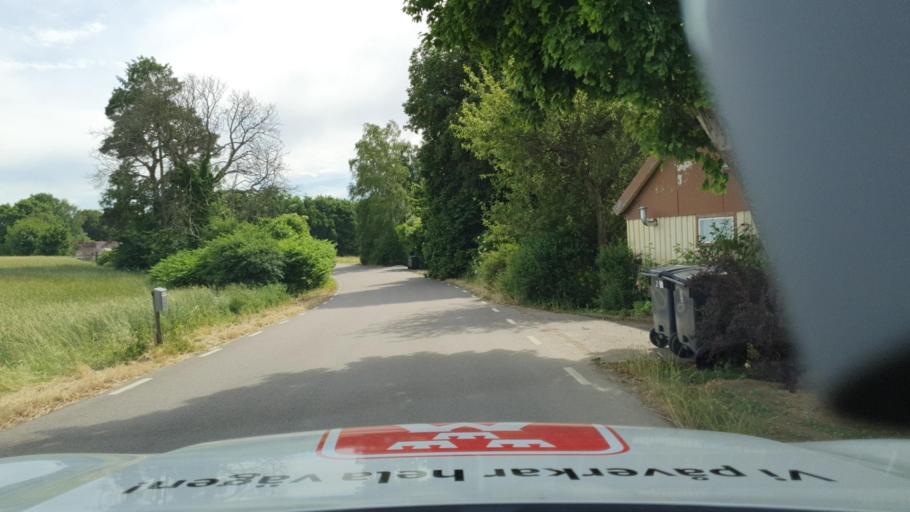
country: SE
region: Skane
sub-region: Tomelilla Kommun
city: Tomelilla
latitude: 55.6648
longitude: 13.9068
